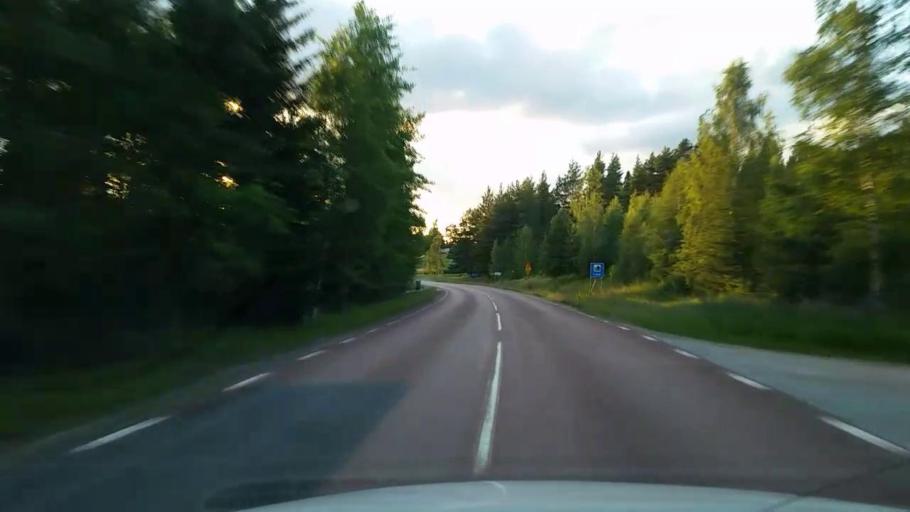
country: SE
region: Vaesternorrland
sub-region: Ange Kommun
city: Ange
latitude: 62.1515
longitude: 15.6819
